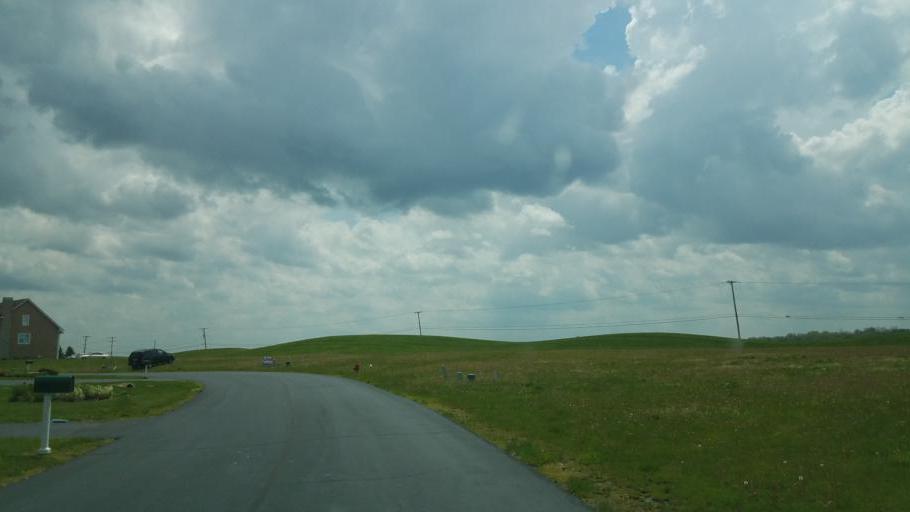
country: US
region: Ohio
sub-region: Perry County
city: Thornport
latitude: 39.9177
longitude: -82.4270
